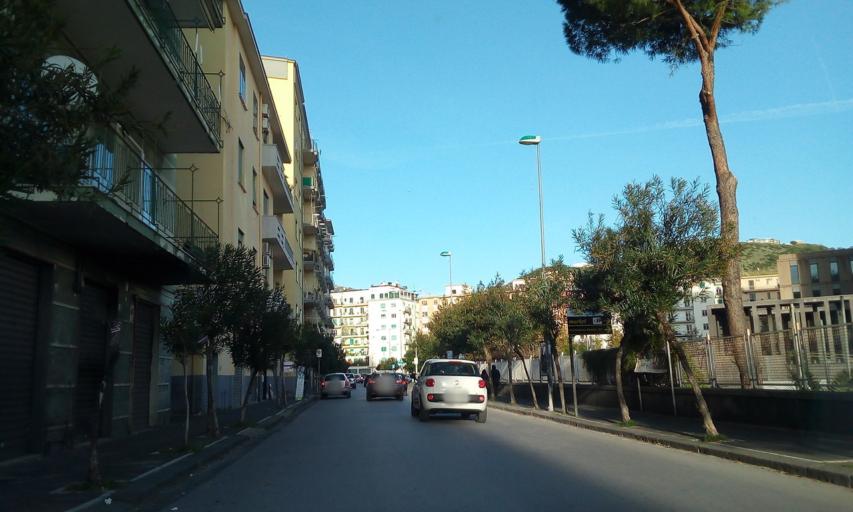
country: IT
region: Campania
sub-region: Provincia di Salerno
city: Salerno
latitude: 40.6791
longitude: 14.7728
